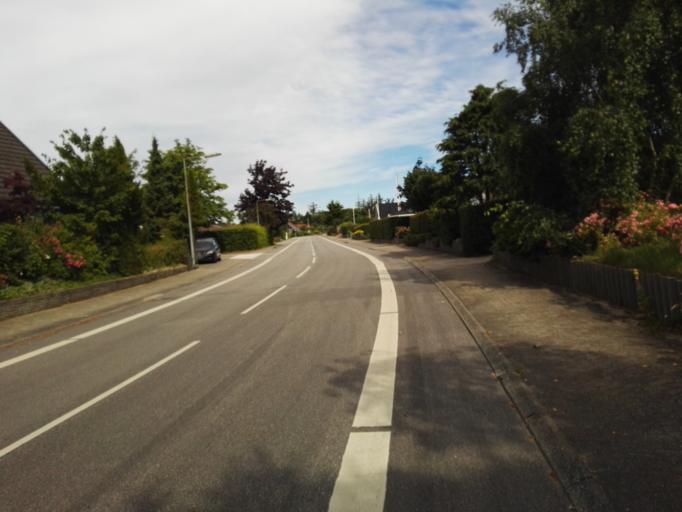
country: DK
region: Capital Region
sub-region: Halsnaes Kommune
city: Hundested
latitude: 55.9704
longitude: 11.8653
